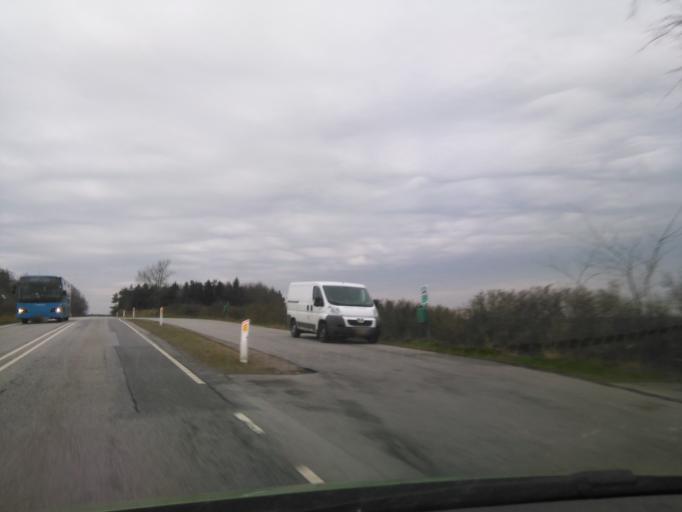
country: DK
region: North Denmark
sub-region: Mariagerfjord Kommune
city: Hadsund
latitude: 56.6823
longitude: 10.0904
